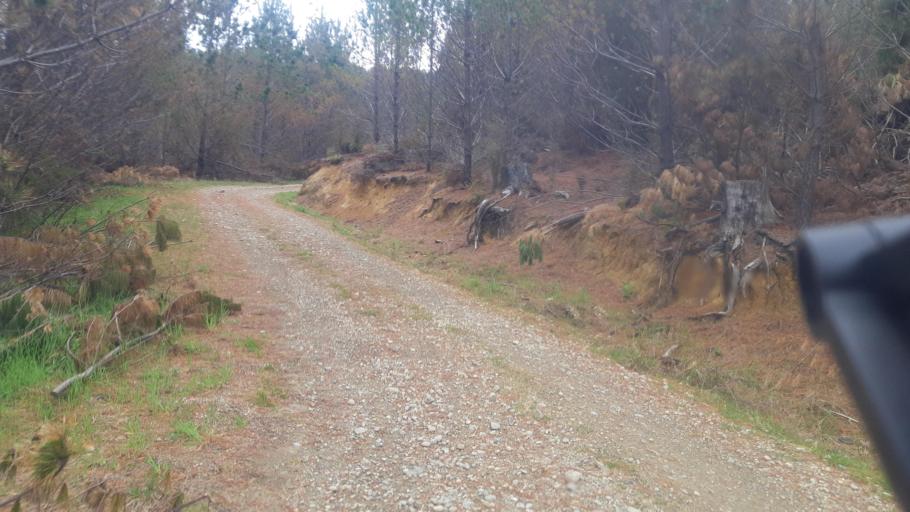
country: NZ
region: Tasman
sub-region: Tasman District
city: Wakefield
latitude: -41.7632
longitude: 172.8033
